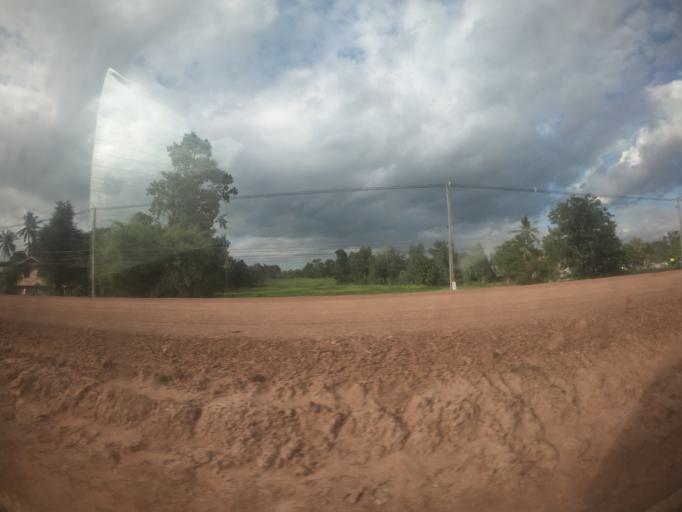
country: TH
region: Surin
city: Kap Choeng
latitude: 14.4969
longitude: 103.5674
